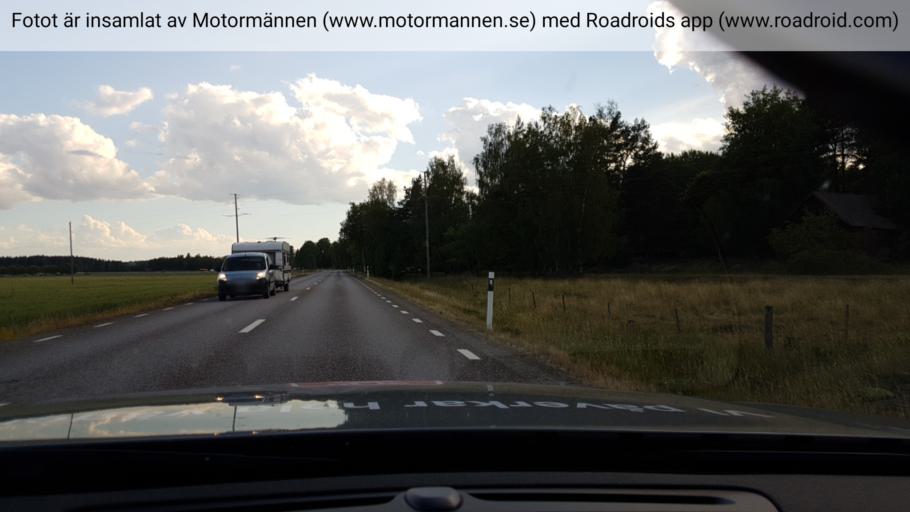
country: SE
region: Uppsala
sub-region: Enkopings Kommun
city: Irsta
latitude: 59.8055
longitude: 16.9101
